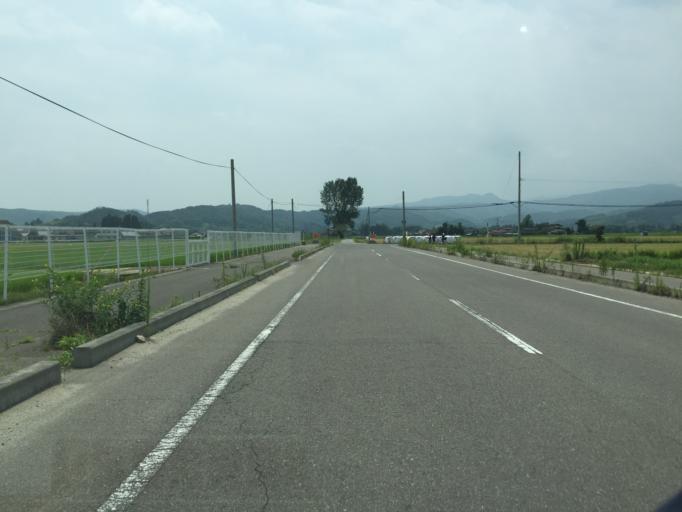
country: JP
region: Fukushima
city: Fukushima-shi
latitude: 37.7224
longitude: 140.4458
